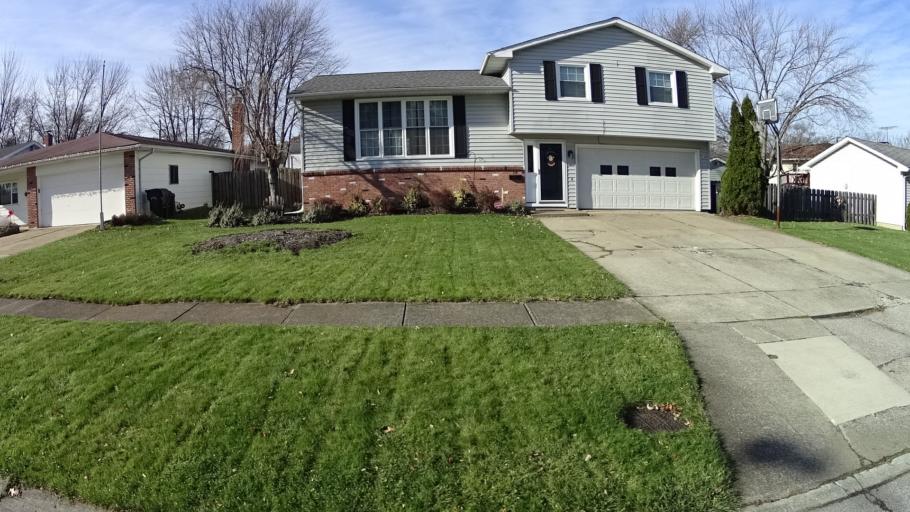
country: US
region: Ohio
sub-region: Lorain County
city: Sheffield
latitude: 41.4019
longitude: -82.0784
